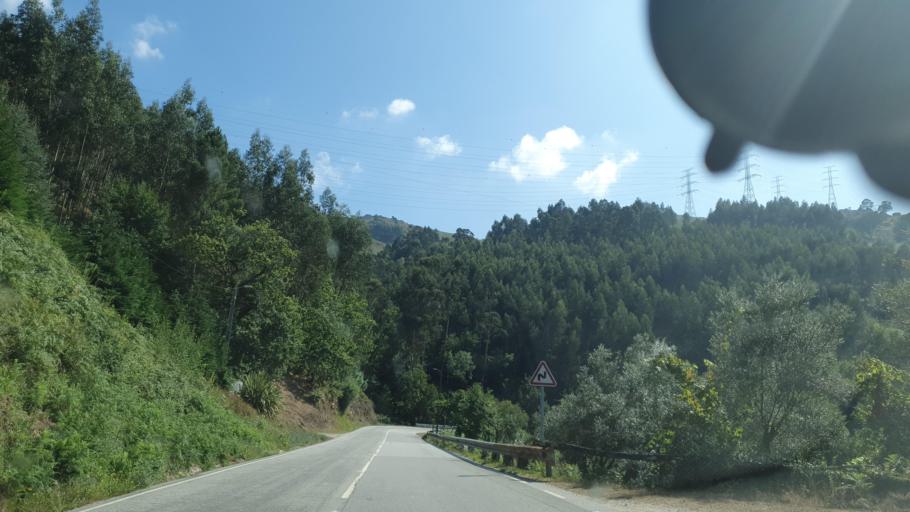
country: PT
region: Braga
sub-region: Vieira do Minho
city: Vieira do Minho
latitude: 41.6739
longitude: -8.1407
